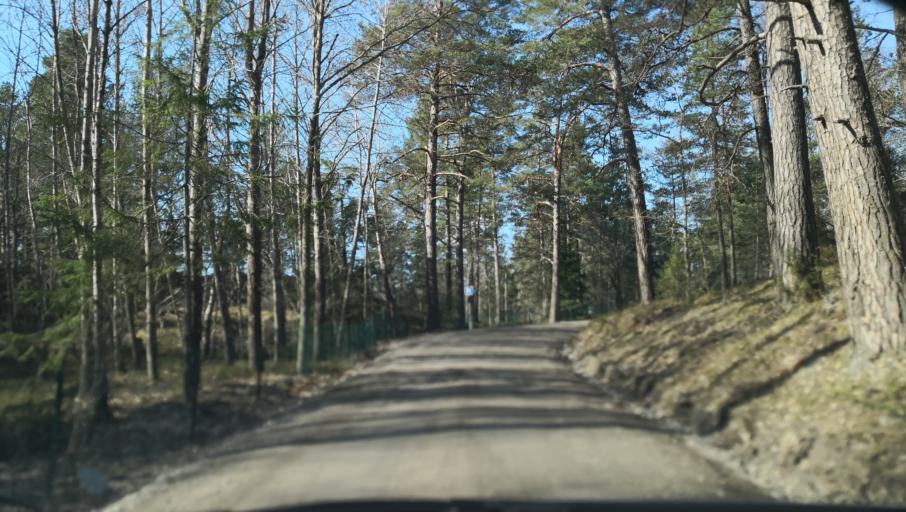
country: SE
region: Stockholm
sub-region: Varmdo Kommun
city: Gustavsberg
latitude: 59.2929
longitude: 18.3627
